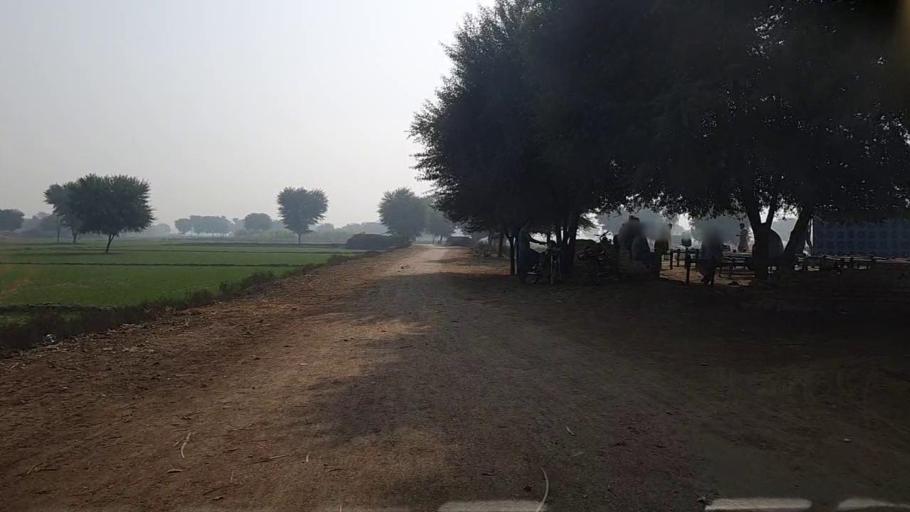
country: PK
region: Sindh
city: Setharja Old
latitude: 27.1508
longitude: 68.4660
